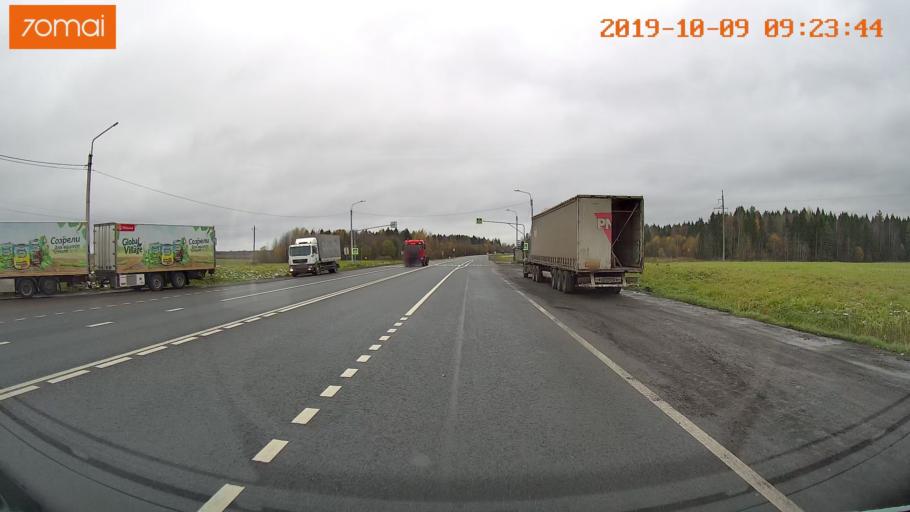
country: RU
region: Vologda
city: Vologda
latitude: 59.0730
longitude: 40.0264
